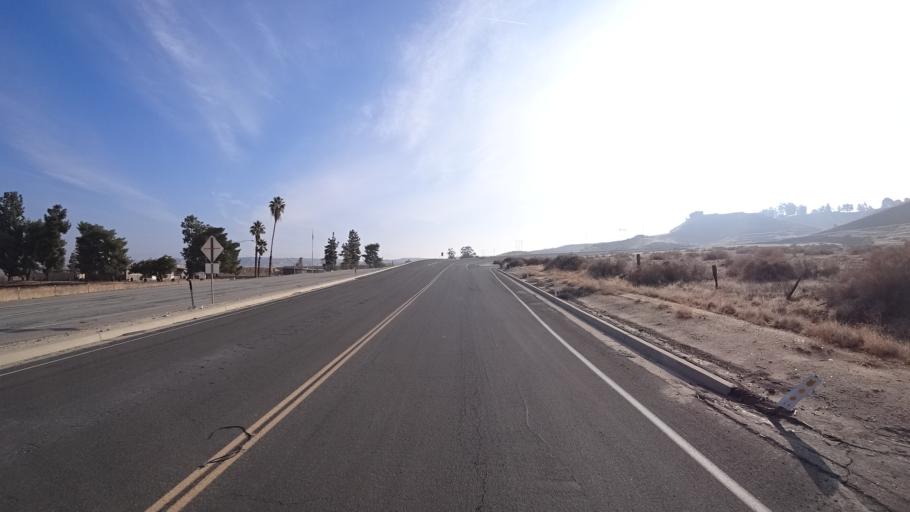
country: US
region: California
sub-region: Kern County
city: Oildale
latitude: 35.4184
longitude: -118.9616
